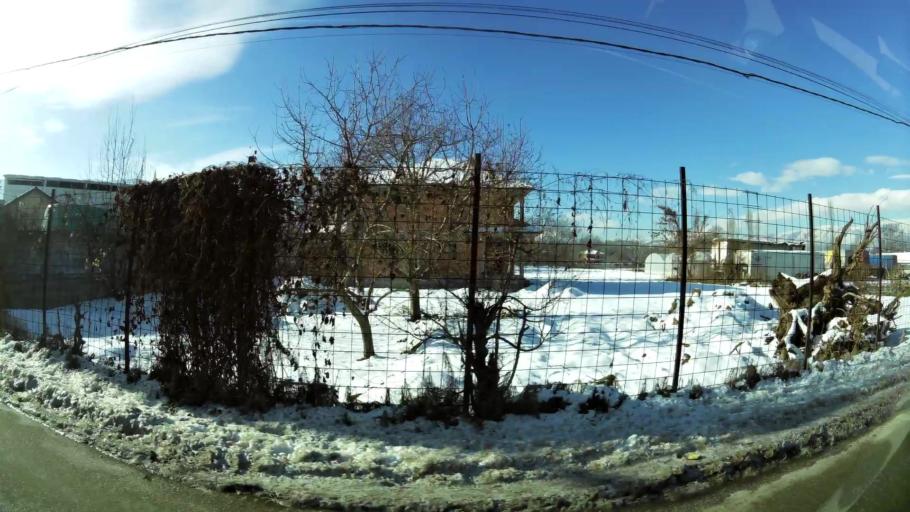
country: MK
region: Saraj
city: Saraj
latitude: 41.9976
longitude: 21.3431
